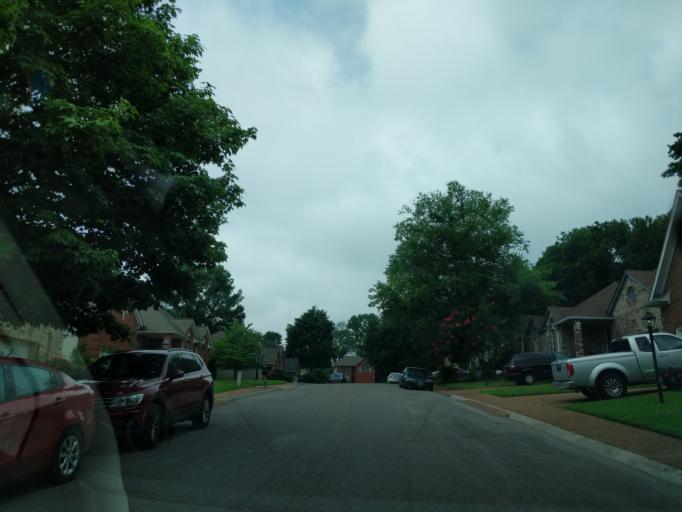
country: US
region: Tennessee
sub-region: Davidson County
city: Lakewood
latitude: 36.1740
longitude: -86.6171
